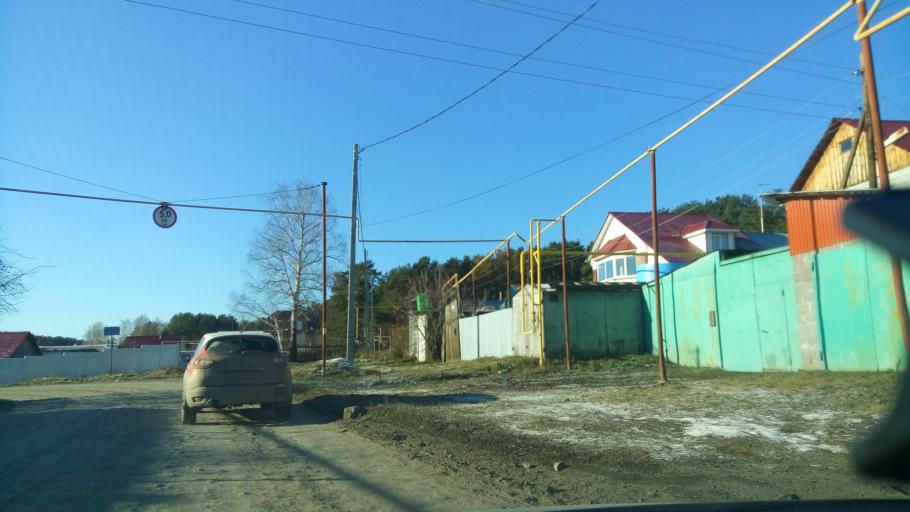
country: RU
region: Sverdlovsk
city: Gornyy Shchit
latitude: 56.7150
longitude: 60.5142
